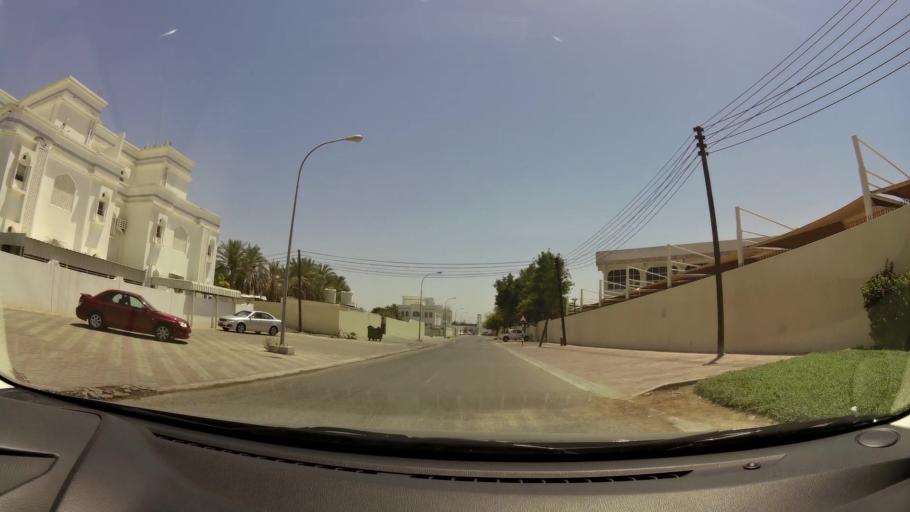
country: OM
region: Muhafazat Masqat
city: As Sib al Jadidah
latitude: 23.6159
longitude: 58.2311
